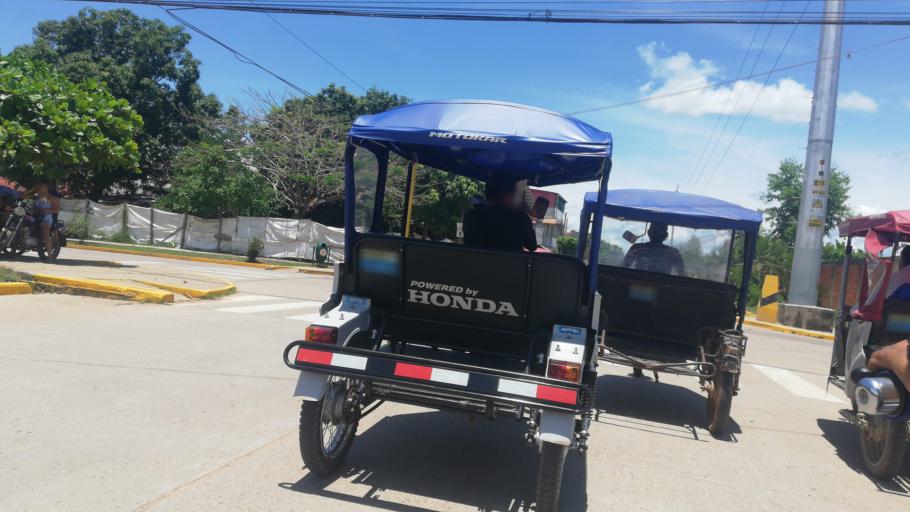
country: PE
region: Ucayali
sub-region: Provincia de Coronel Portillo
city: Puerto Callao
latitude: -8.3594
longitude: -74.5736
